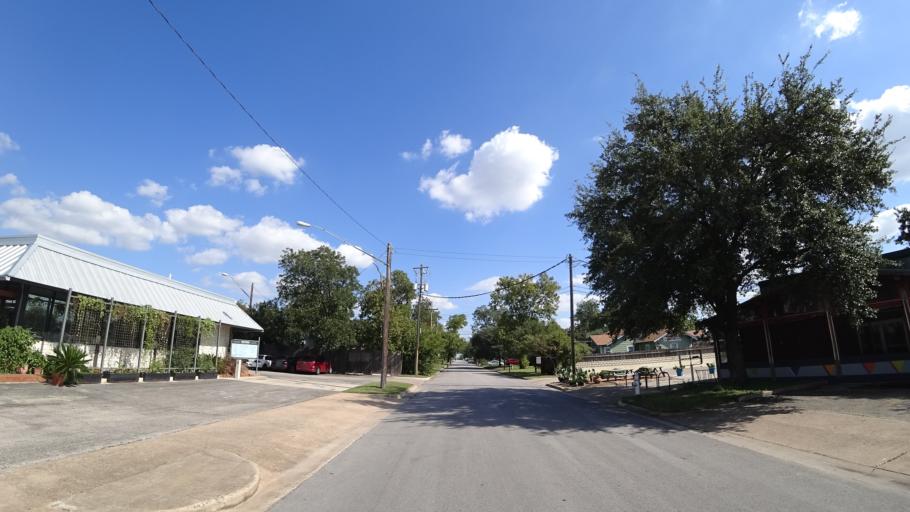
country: US
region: Texas
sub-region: Travis County
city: Austin
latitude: 30.3130
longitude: -97.7150
